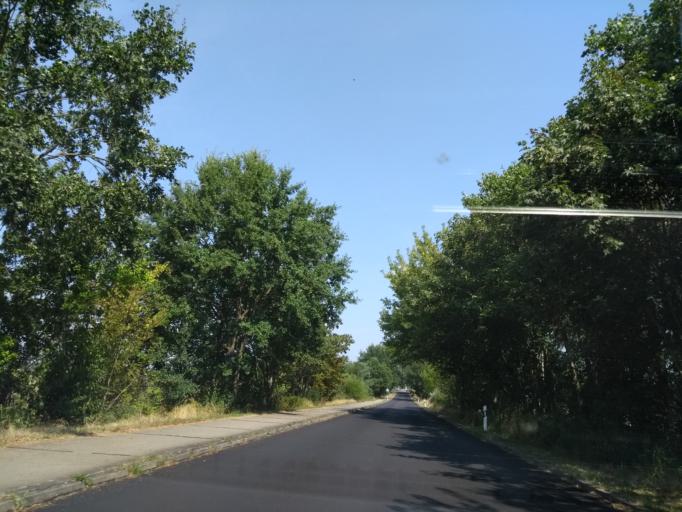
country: DE
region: Brandenburg
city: Lubbenau
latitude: 51.8416
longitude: 13.9381
